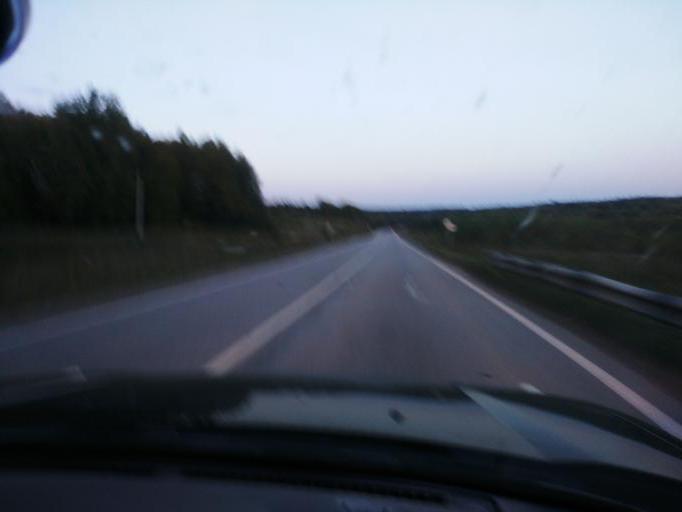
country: RU
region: Perm
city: Verkhnechusovskiye Gorodki
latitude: 58.2818
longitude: 56.9048
